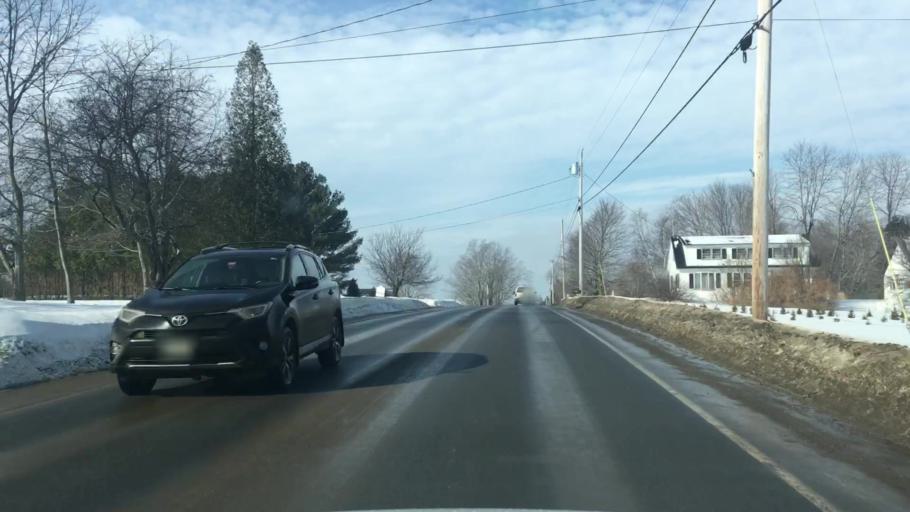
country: US
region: Maine
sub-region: Penobscot County
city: Hermon
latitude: 44.8462
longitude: -68.8699
